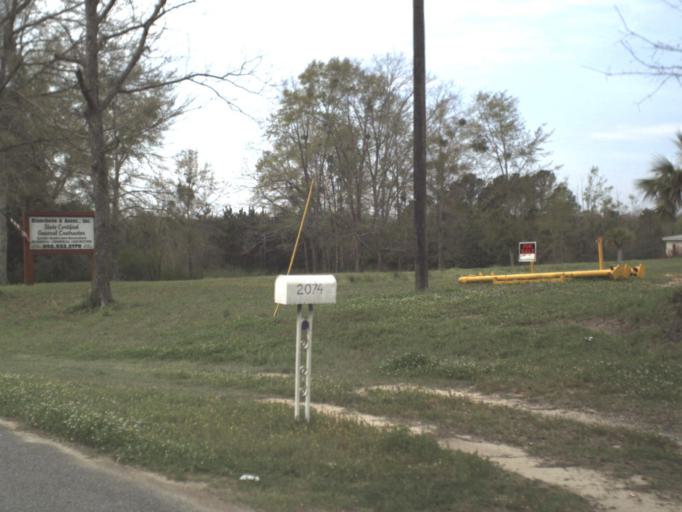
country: US
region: Florida
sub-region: Holmes County
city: Bonifay
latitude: 30.8339
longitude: -85.6669
